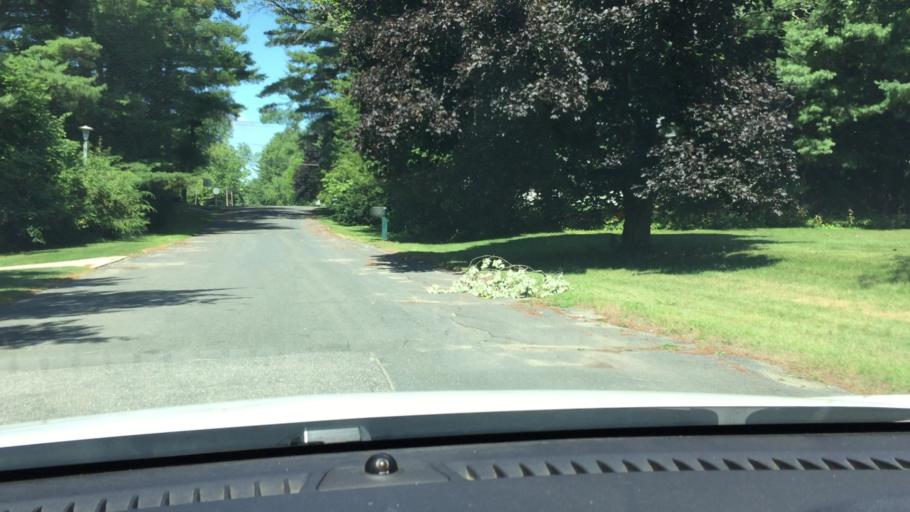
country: US
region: Massachusetts
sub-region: Berkshire County
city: Pittsfield
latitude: 42.4321
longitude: -73.2366
